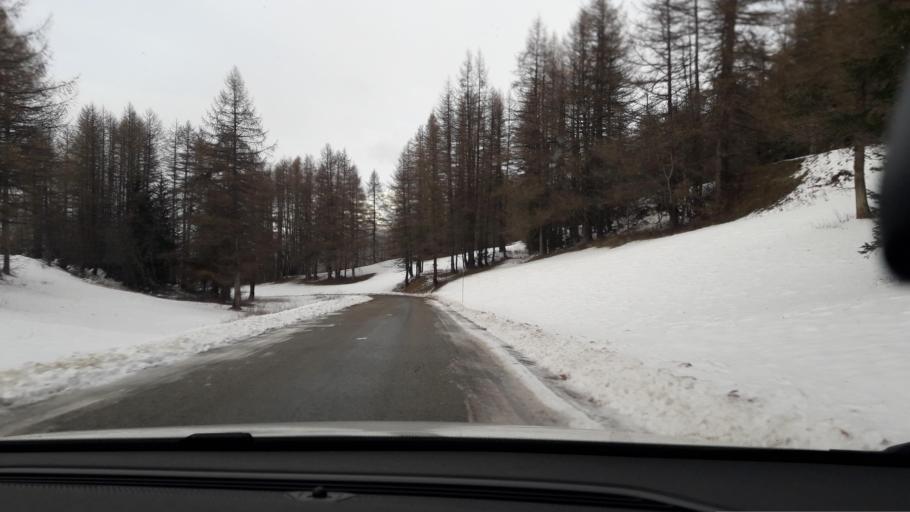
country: FR
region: Rhone-Alpes
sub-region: Departement de la Savoie
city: Saint-Michel-de-Maurienne
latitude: 45.2165
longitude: 6.4239
